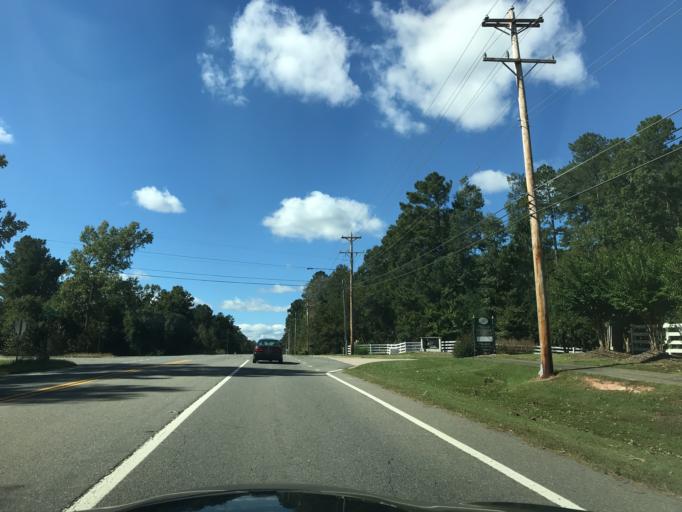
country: US
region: North Carolina
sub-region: Durham County
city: Gorman
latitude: 35.9773
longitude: -78.7751
